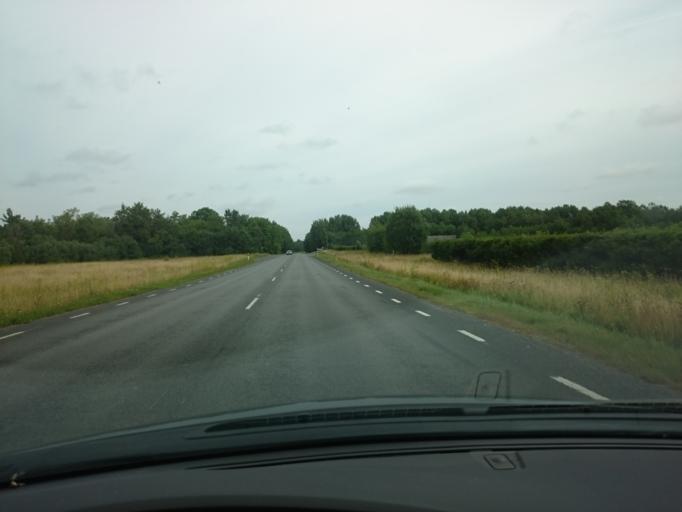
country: EE
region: Laeaene
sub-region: Ridala Parish
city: Uuemoisa
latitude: 58.9751
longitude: 23.6785
